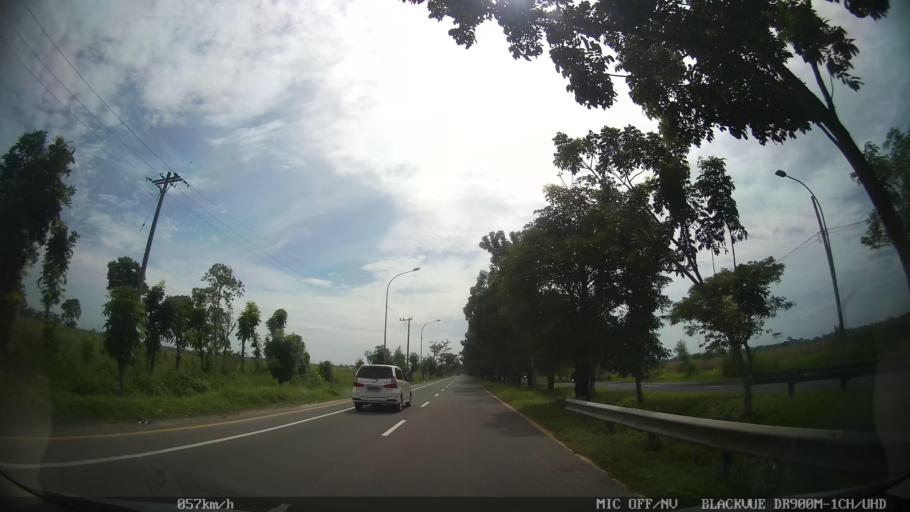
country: ID
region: North Sumatra
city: Percut
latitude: 3.5987
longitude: 98.8155
